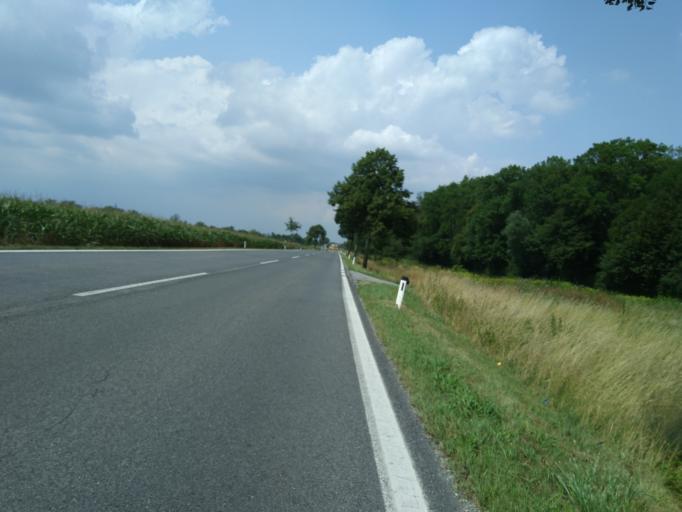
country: AT
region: Lower Austria
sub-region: Politischer Bezirk Ganserndorf
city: Ganserndorf
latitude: 48.3492
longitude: 16.7113
